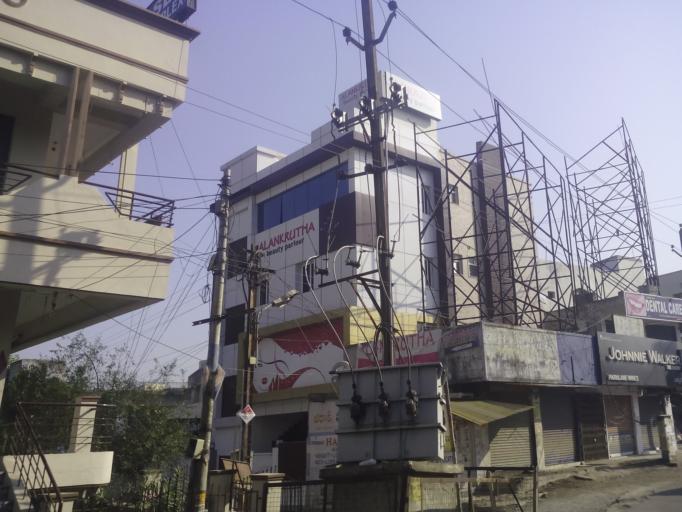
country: IN
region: Telangana
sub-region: Warangal
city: Warangal
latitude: 17.9894
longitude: 79.5984
